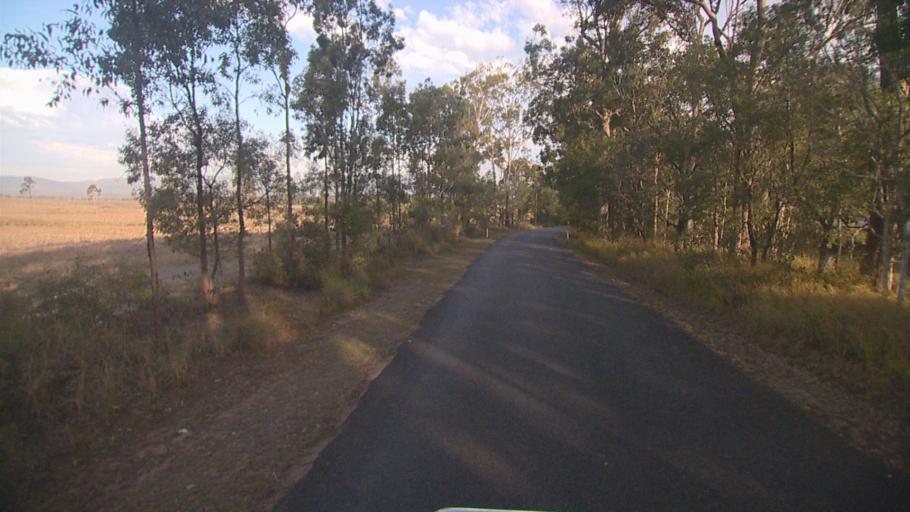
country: AU
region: Queensland
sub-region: Logan
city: Chambers Flat
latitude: -27.8406
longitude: 153.1192
